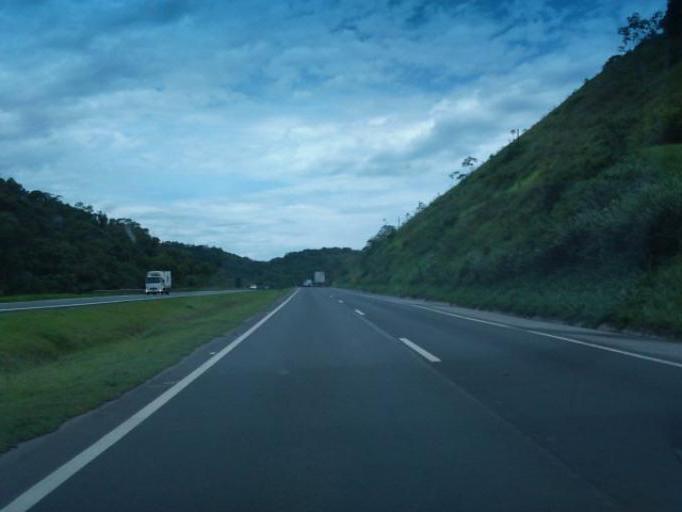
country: BR
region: Sao Paulo
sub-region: Miracatu
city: Miracatu
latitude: -24.2273
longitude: -47.3635
